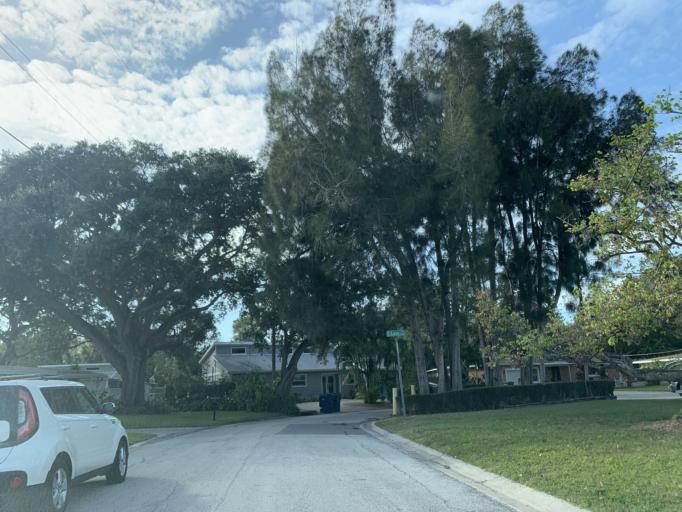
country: US
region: Florida
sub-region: Hillsborough County
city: Tampa
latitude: 27.8960
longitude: -82.5135
